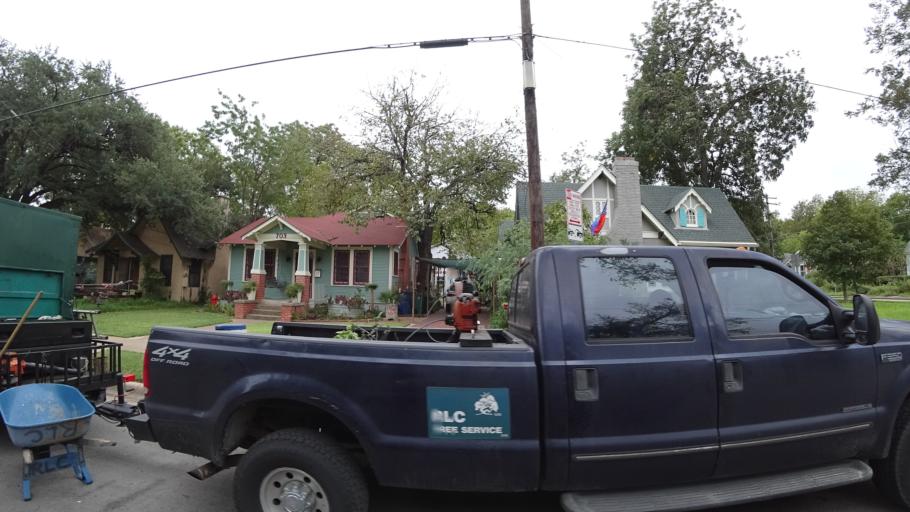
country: US
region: Texas
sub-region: Travis County
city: Austin
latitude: 30.2942
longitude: -97.7300
